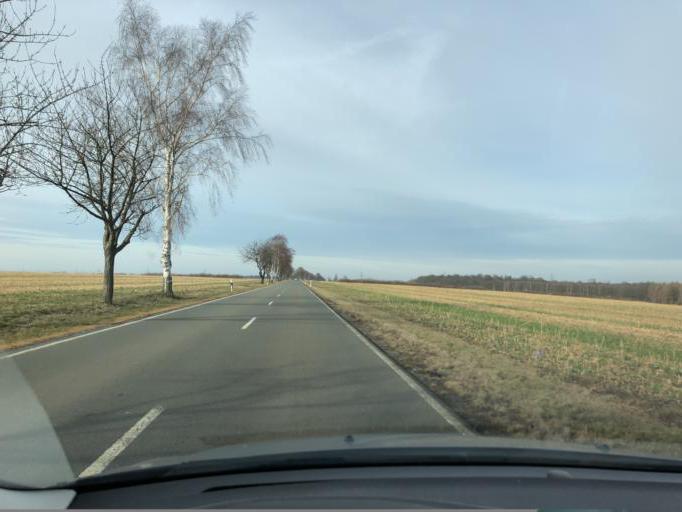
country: DE
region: Saxony-Anhalt
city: Bad Bibra
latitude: 51.1853
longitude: 11.5355
